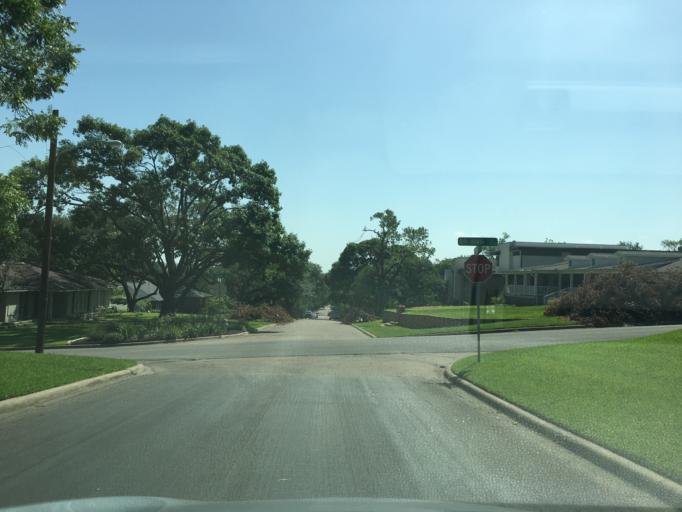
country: US
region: Texas
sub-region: Dallas County
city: University Park
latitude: 32.9046
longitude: -96.7767
